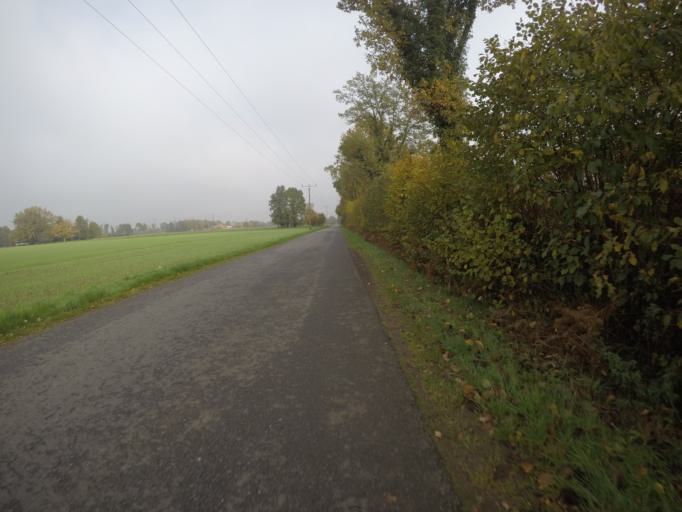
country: DE
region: North Rhine-Westphalia
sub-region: Regierungsbezirk Dusseldorf
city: Bocholt
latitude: 51.8215
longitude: 6.5647
